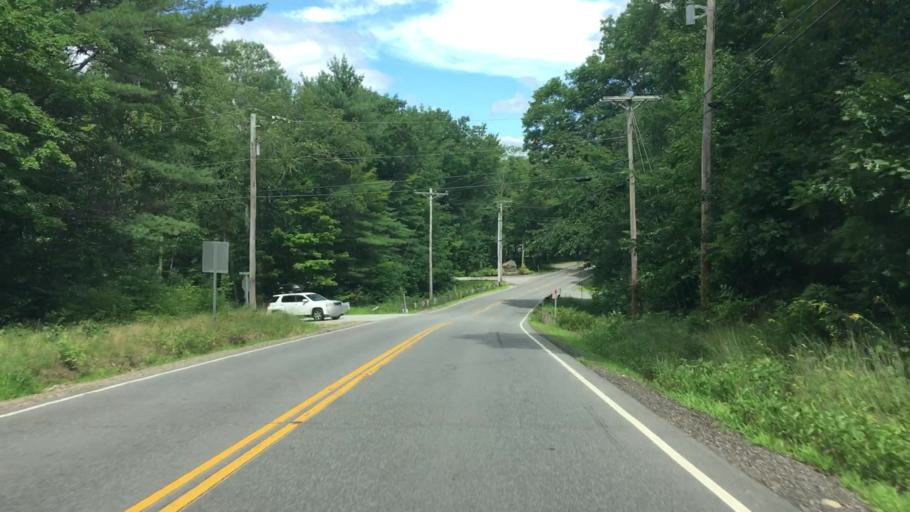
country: US
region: New Hampshire
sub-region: Belknap County
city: Meredith
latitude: 43.6058
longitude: -71.5236
